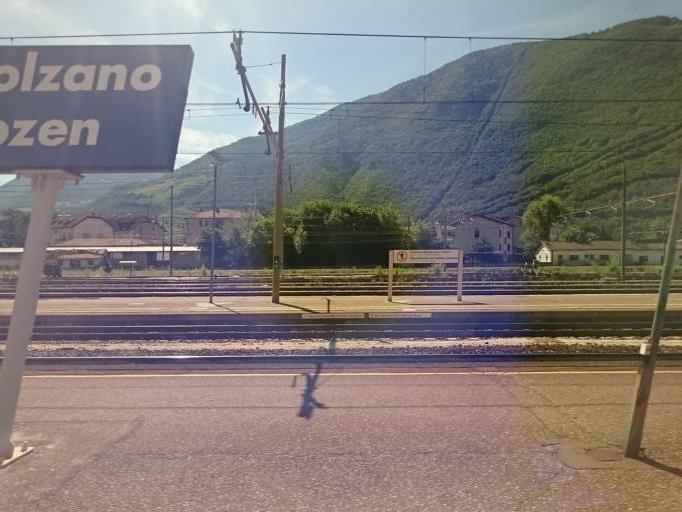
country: IT
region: Trentino-Alto Adige
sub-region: Bolzano
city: Bolzano
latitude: 46.4981
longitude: 11.3617
